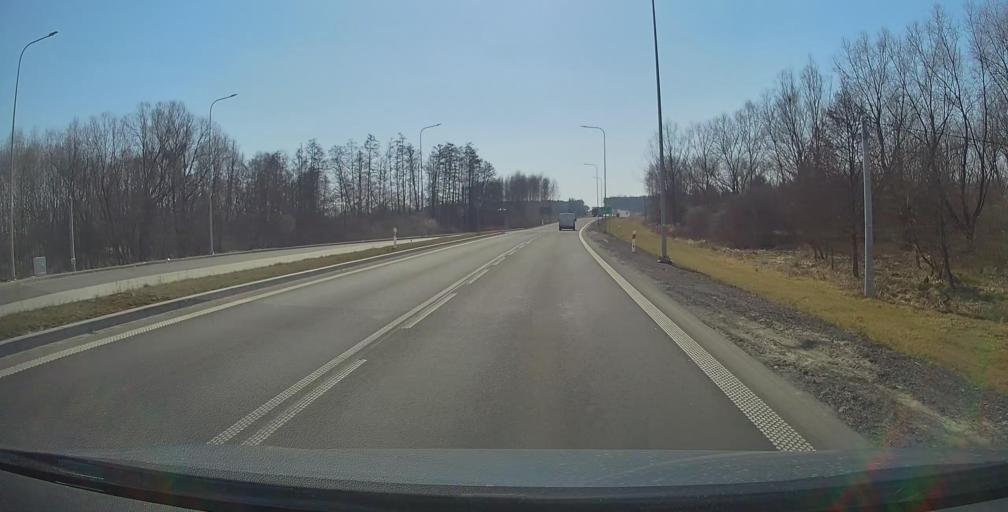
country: PL
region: Subcarpathian Voivodeship
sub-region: Powiat nizanski
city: Raclawice
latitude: 50.5170
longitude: 22.1719
